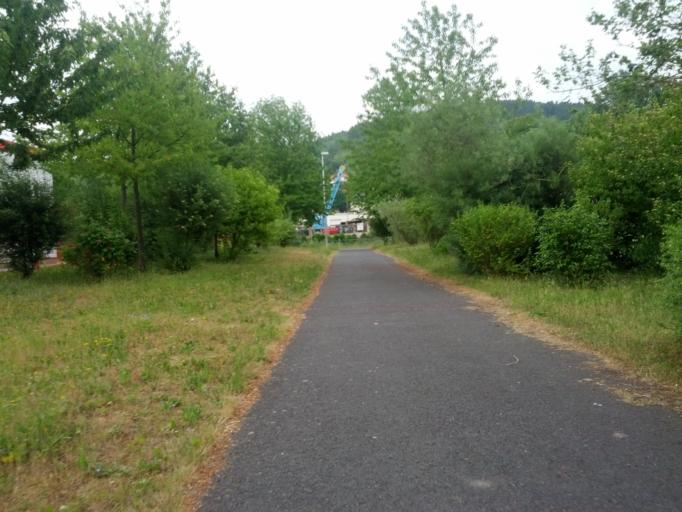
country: DE
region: Thuringia
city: Eisenach
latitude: 50.9687
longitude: 10.3457
